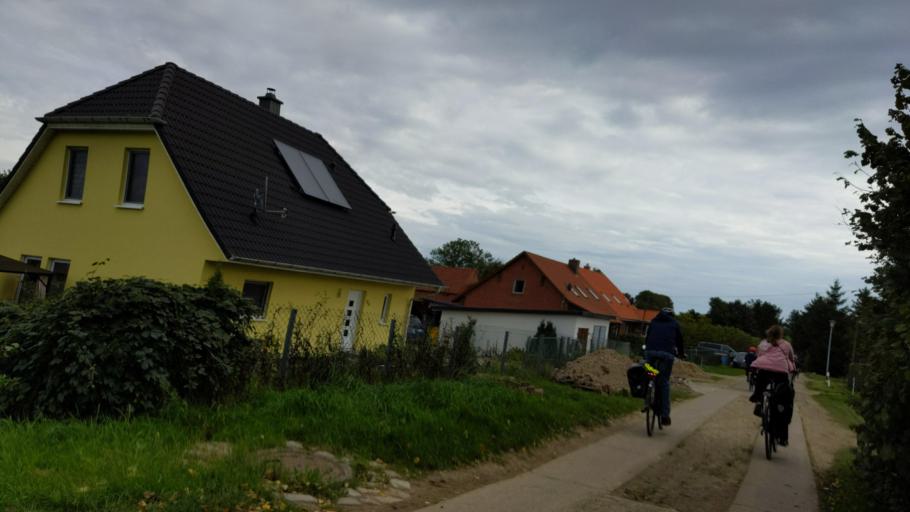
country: DE
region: Mecklenburg-Vorpommern
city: Schlagsdorf
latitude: 53.7310
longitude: 10.8177
